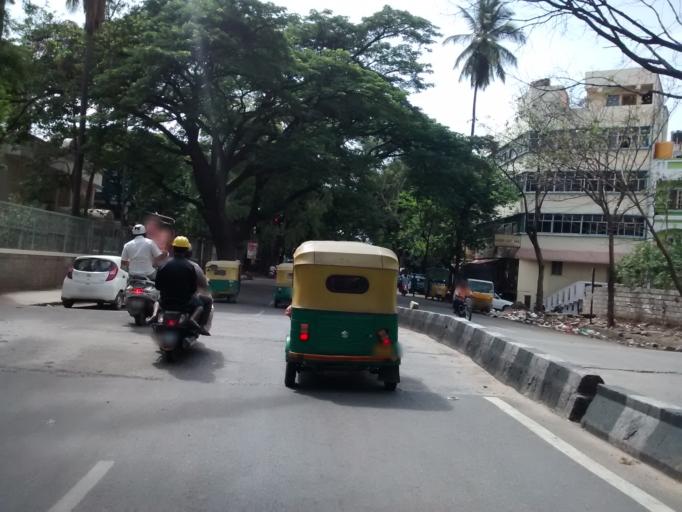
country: IN
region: Karnataka
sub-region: Bangalore Urban
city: Bangalore
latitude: 12.9942
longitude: 77.5555
